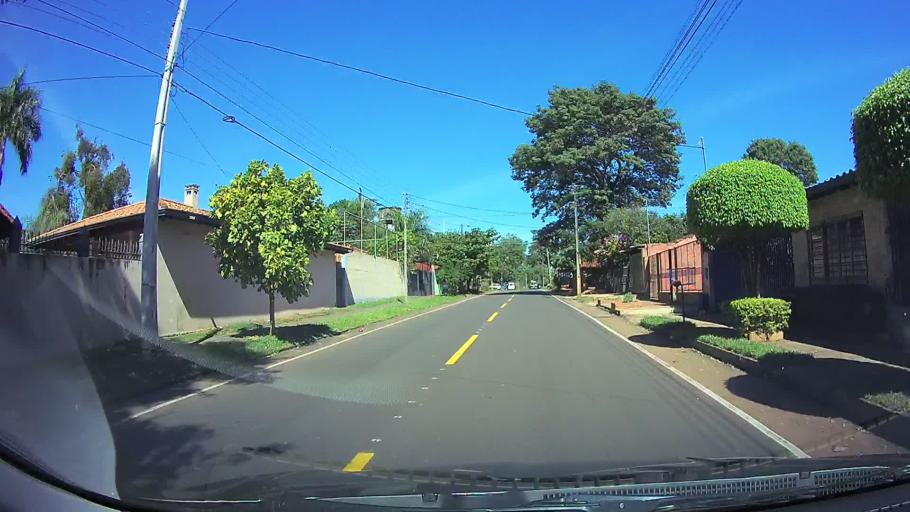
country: PY
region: Central
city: San Lorenzo
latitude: -25.2688
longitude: -57.4720
